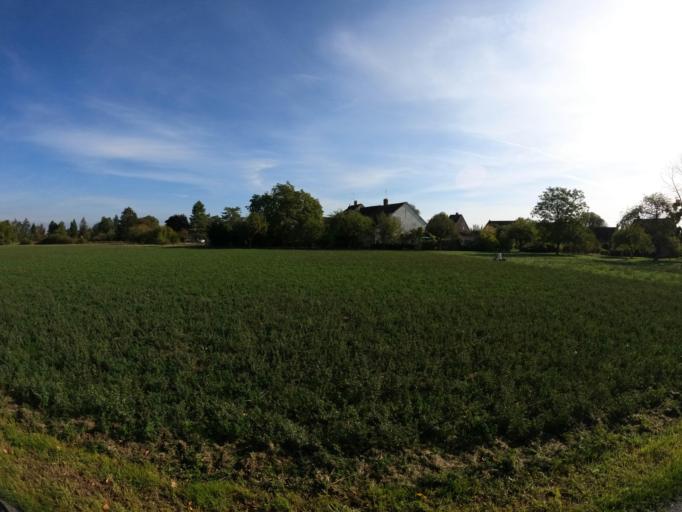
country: FR
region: Franche-Comte
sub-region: Departement du Jura
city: Bletterans
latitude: 46.7468
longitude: 5.4917
